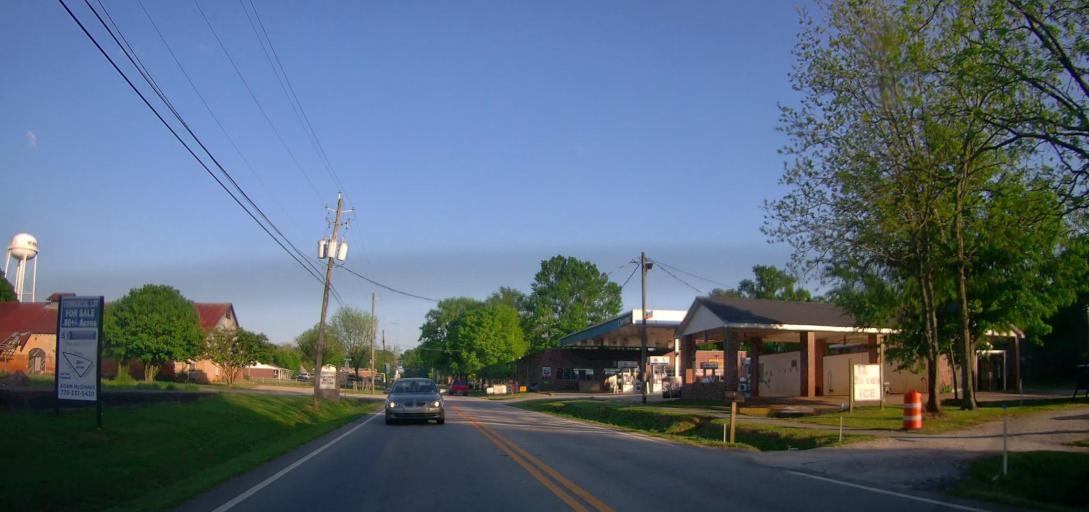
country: US
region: Georgia
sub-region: Walton County
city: Social Circle
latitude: 33.5177
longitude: -83.6966
